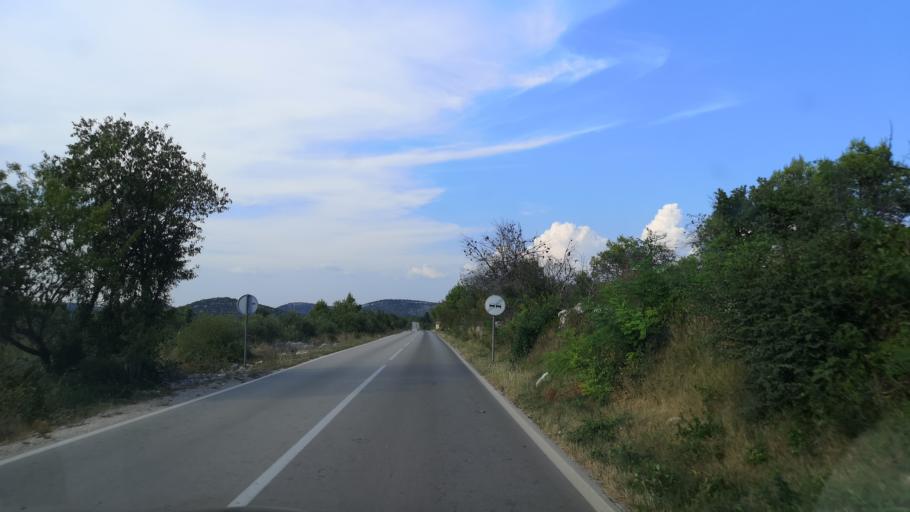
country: HR
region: Sibensko-Kniniska
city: Vodice
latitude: 43.8032
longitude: 15.7736
